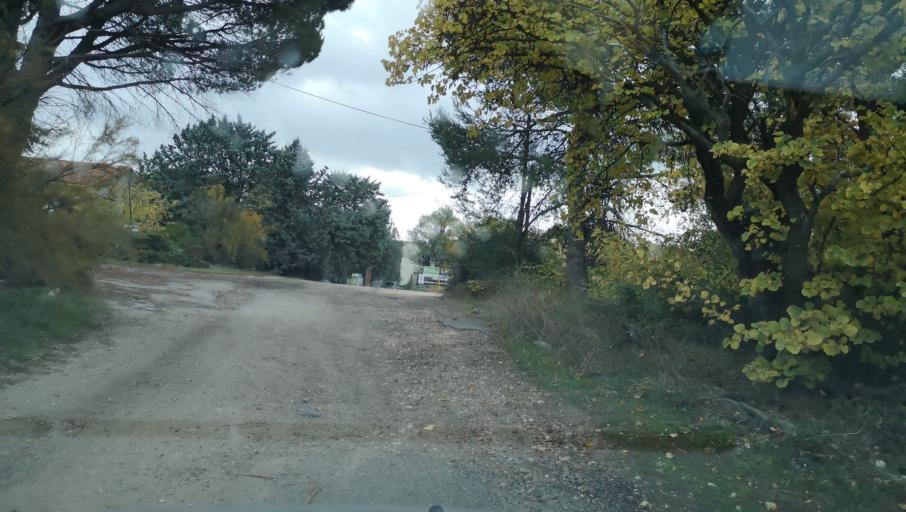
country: FR
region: Provence-Alpes-Cote d'Azur
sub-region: Departement des Bouches-du-Rhone
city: Rousset
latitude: 43.4651
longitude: 5.6120
